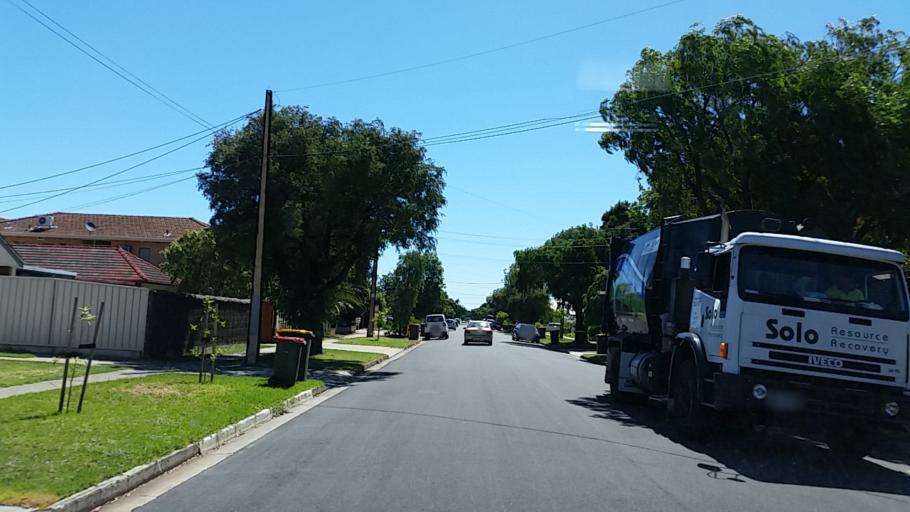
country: AU
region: South Australia
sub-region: Marion
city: South Plympton
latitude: -34.9759
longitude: 138.5633
